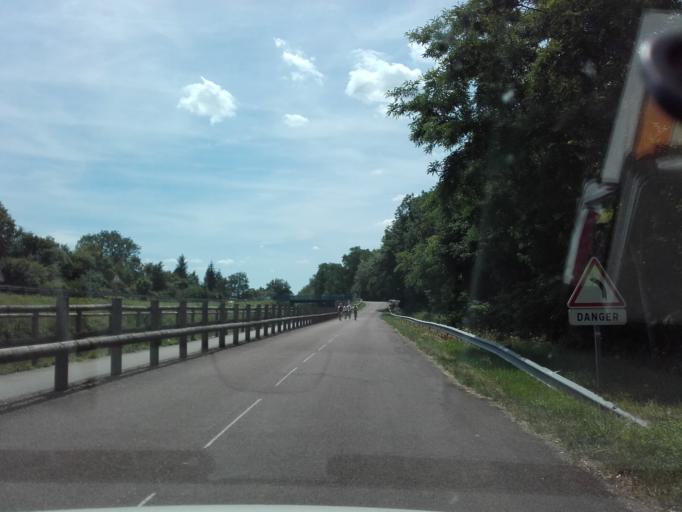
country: FR
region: Bourgogne
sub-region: Departement de Saone-et-Loire
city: Rully
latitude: 46.9025
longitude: 4.6935
